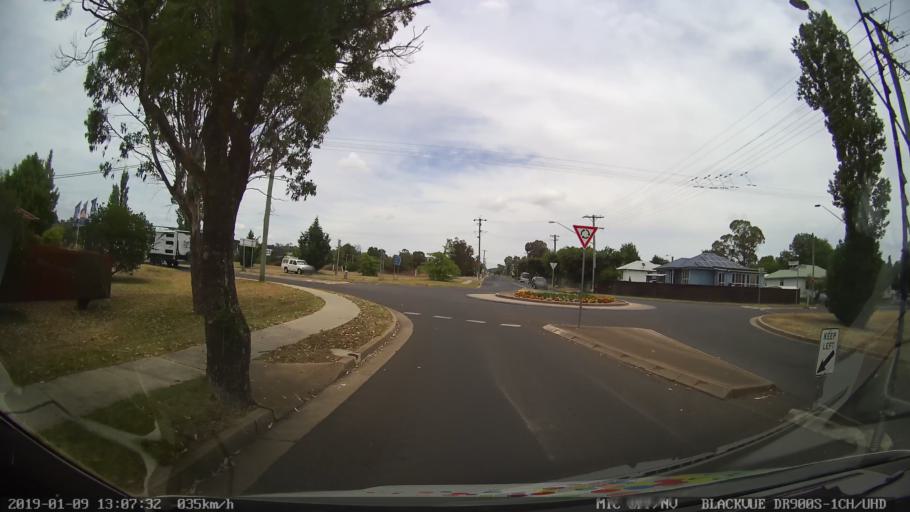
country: AU
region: New South Wales
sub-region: Armidale Dumaresq
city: Armidale
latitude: -30.5201
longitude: 151.6787
